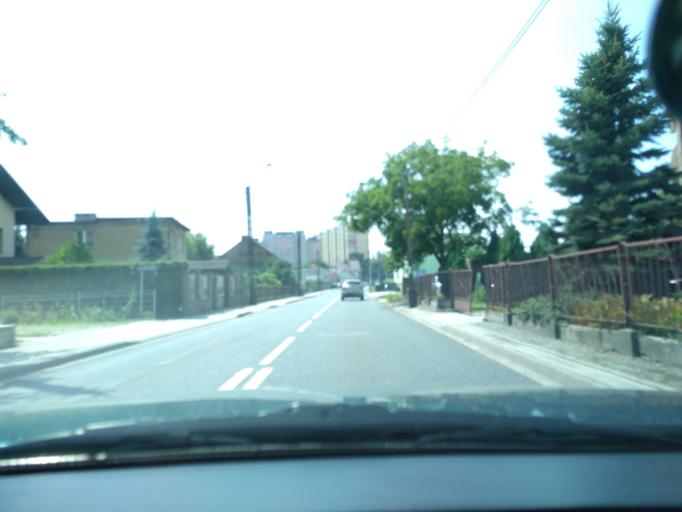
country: PL
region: Silesian Voivodeship
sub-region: Powiat raciborski
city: Raciborz
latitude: 50.0902
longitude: 18.2000
